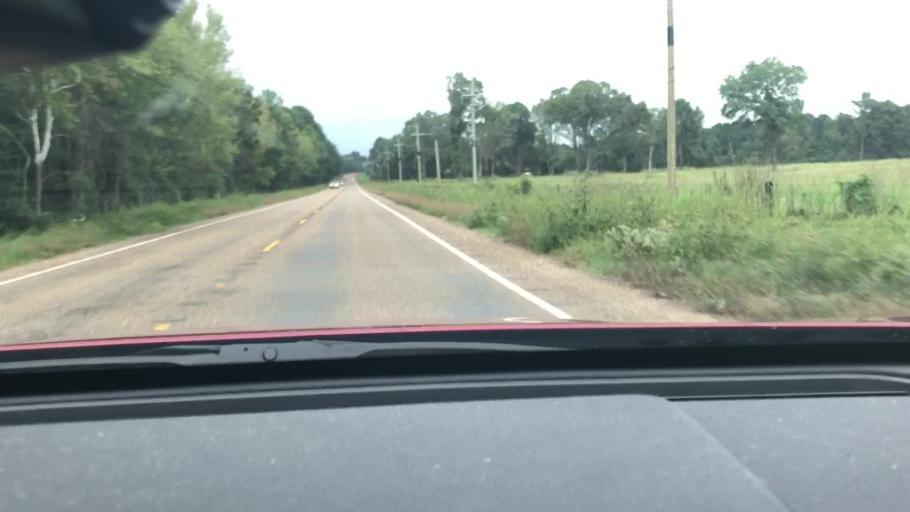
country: US
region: Texas
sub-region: Bowie County
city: Wake Village
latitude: 33.3765
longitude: -94.1002
